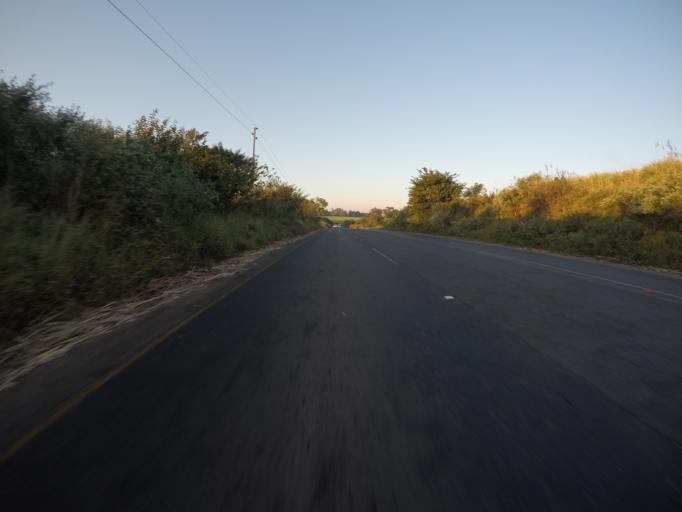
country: ZA
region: KwaZulu-Natal
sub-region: uThungulu District Municipality
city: Empangeni
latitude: -28.7912
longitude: 31.8971
